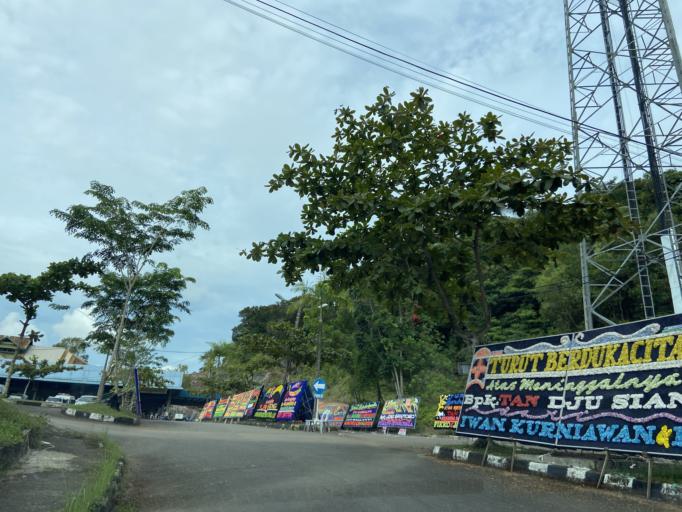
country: SG
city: Singapore
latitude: 1.1209
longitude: 104.0079
